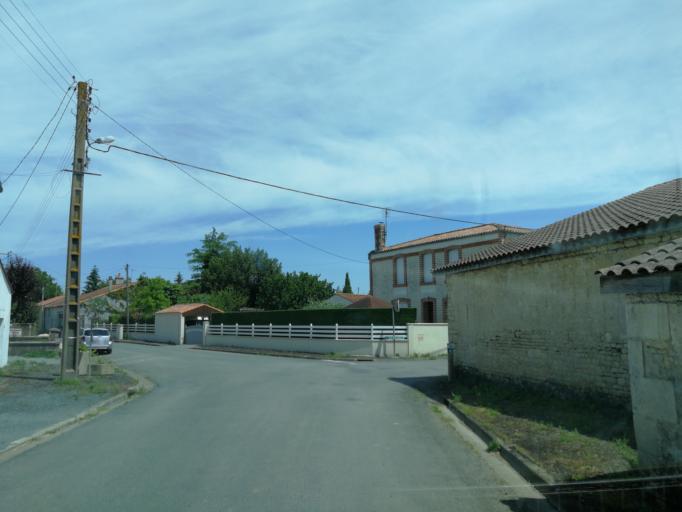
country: FR
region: Pays de la Loire
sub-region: Departement de la Vendee
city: Le Langon
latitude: 46.4175
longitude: -0.9079
